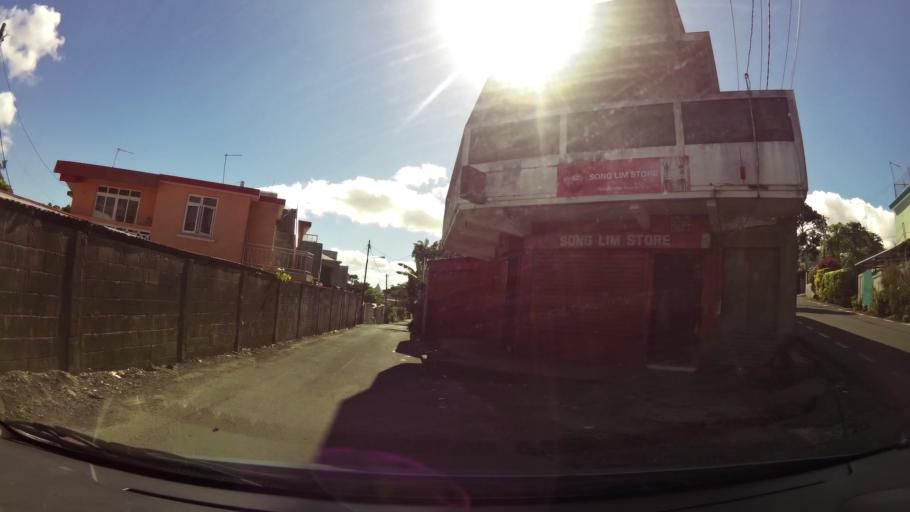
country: MU
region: Plaines Wilhems
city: Curepipe
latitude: -20.3021
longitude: 57.5016
